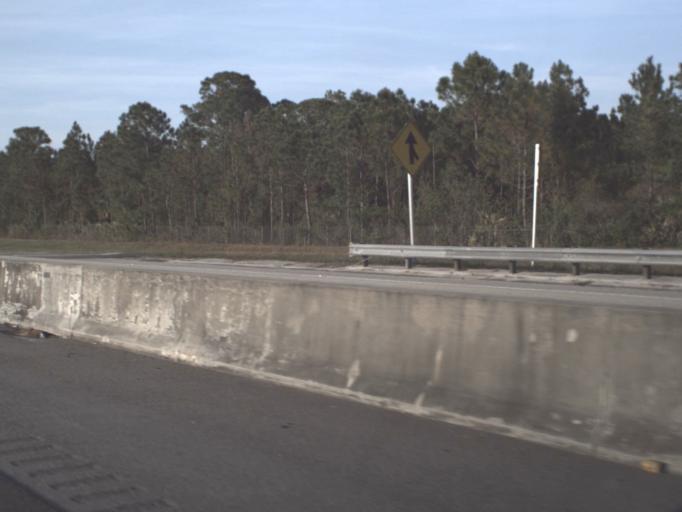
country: US
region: Florida
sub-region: Brevard County
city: Sharpes
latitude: 28.4143
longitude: -80.8202
